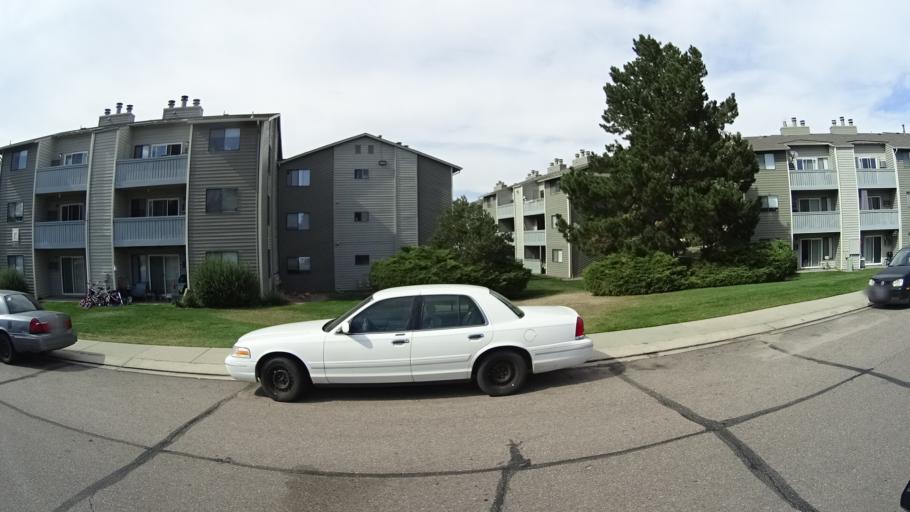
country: US
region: Colorado
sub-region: El Paso County
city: Colorado Springs
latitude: 38.9010
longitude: -104.7771
